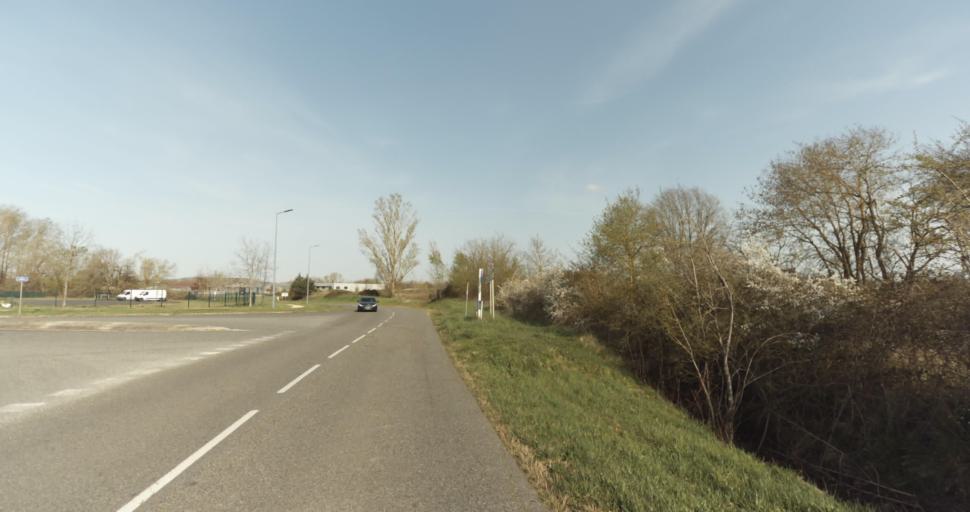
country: FR
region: Midi-Pyrenees
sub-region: Departement du Tarn
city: Saint-Sulpice-la-Pointe
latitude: 43.7675
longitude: 1.7174
